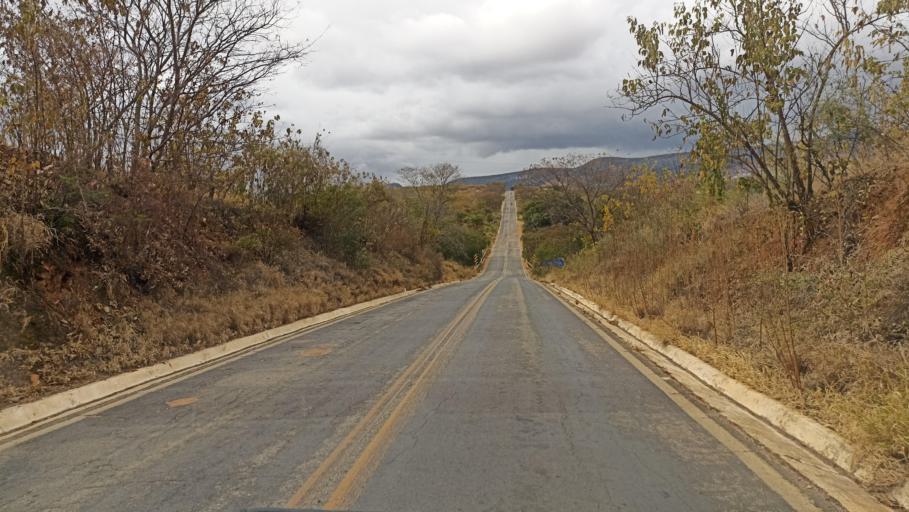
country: BR
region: Minas Gerais
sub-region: Itinga
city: Itinga
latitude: -16.6286
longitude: -41.7894
